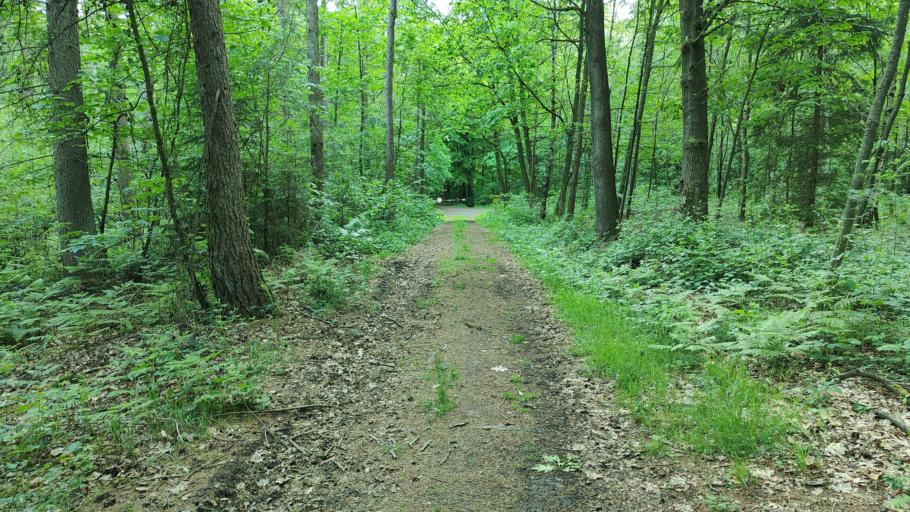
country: BE
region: Wallonia
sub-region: Province de Liege
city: La Calamine
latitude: 50.7074
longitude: 6.0502
